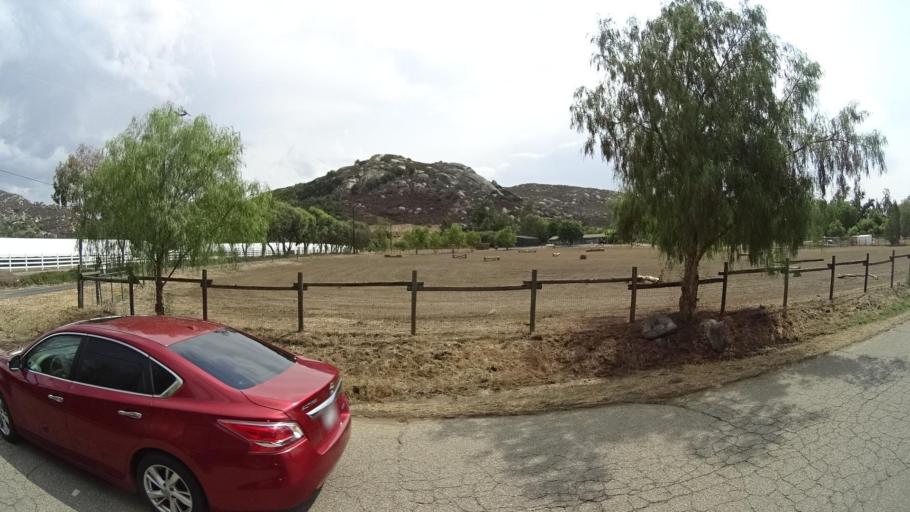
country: US
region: California
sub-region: San Diego County
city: Ramona
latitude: 33.0739
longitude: -116.8393
